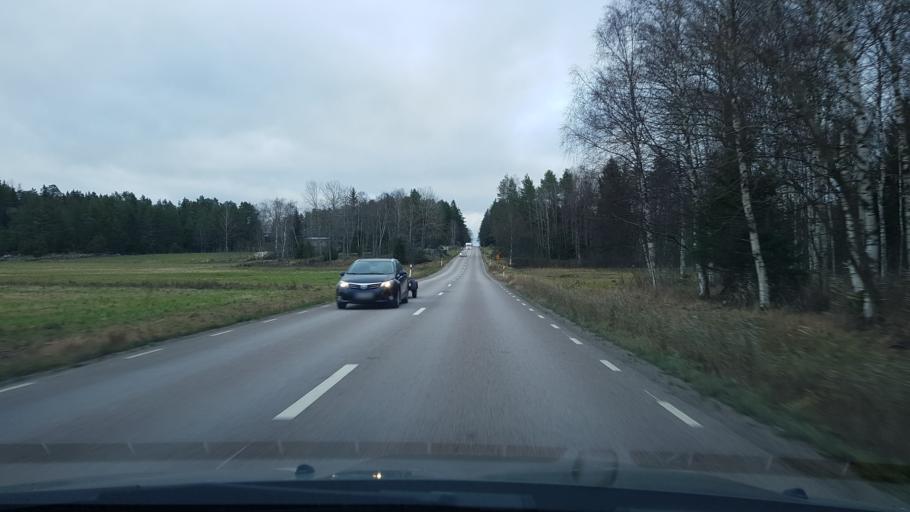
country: SE
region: Uppsala
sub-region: Osthammars Kommun
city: Gimo
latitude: 59.9695
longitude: 18.1262
